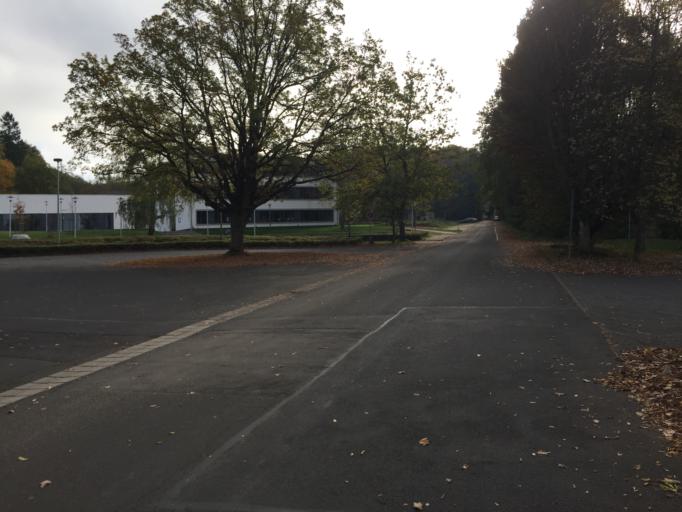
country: DE
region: Hesse
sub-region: Regierungsbezirk Giessen
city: Grunberg
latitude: 50.5885
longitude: 8.9844
